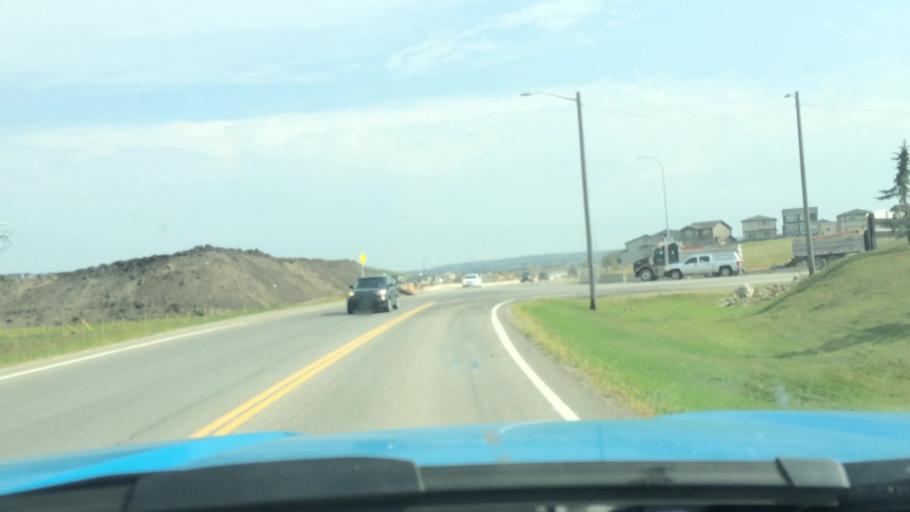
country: CA
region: Alberta
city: Calgary
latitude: 51.1838
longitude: -114.1354
